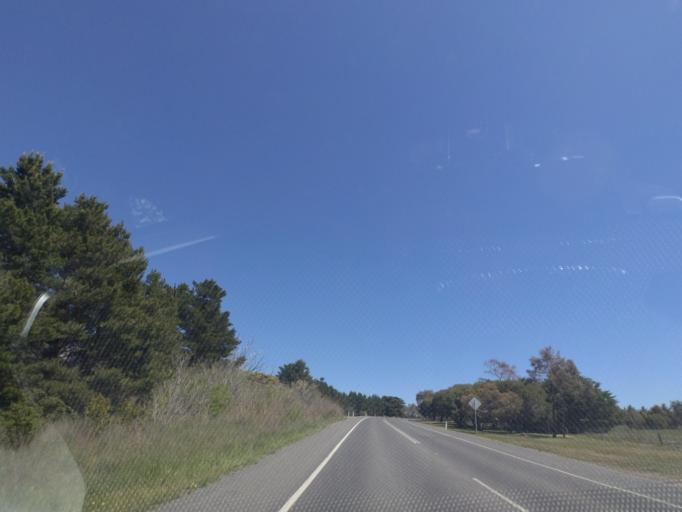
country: AU
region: Victoria
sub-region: Hume
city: Sunbury
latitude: -37.3108
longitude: 144.8478
